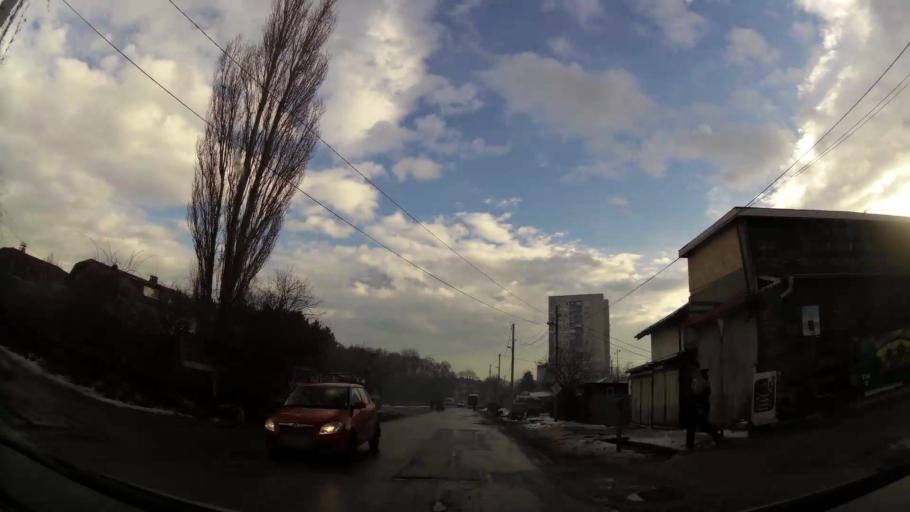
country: BG
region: Sofia-Capital
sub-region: Stolichna Obshtina
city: Sofia
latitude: 42.6986
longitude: 23.2745
